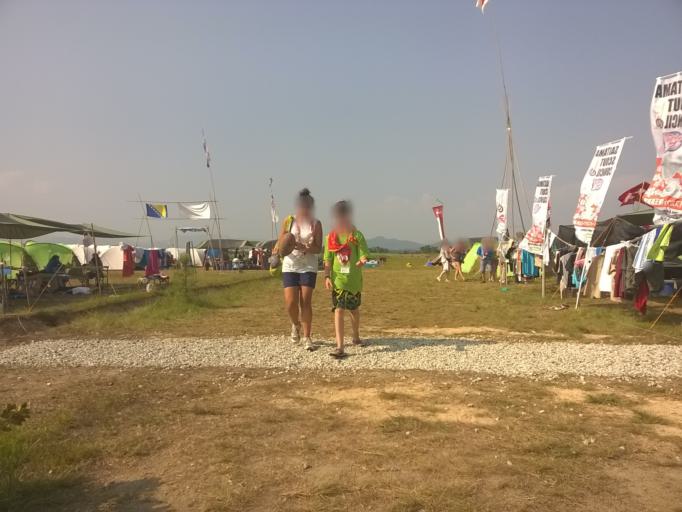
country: JP
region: Yamaguchi
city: Ogori-shimogo
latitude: 34.0220
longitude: 131.3728
